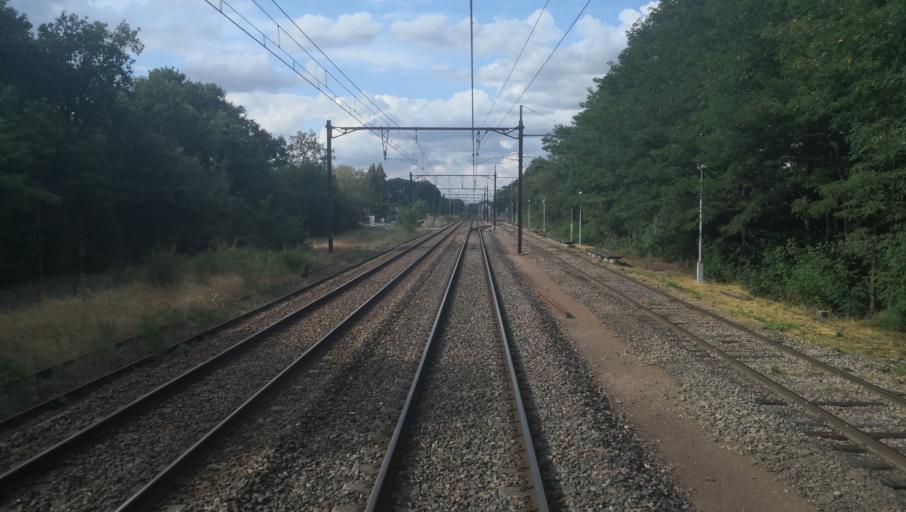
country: FR
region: Centre
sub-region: Departement du Loiret
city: Saint-Cyr-en-Val
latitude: 47.8134
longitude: 1.9464
